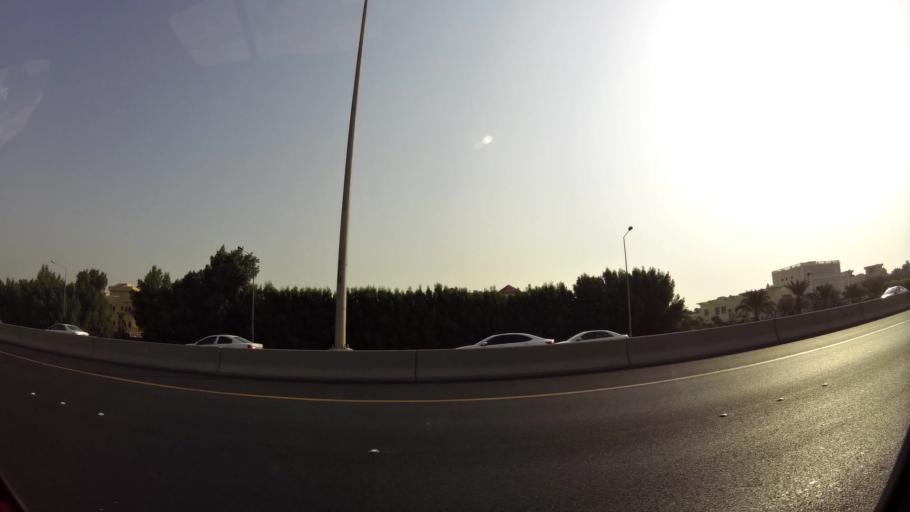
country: KW
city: Al Funaytis
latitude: 29.2070
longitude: 48.1048
